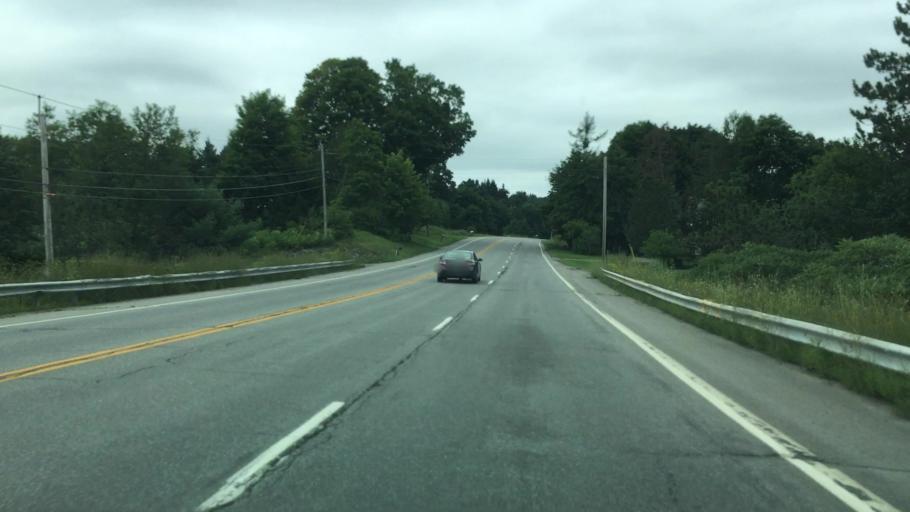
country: US
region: Maine
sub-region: Penobscot County
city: Orrington
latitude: 44.7097
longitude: -68.8471
